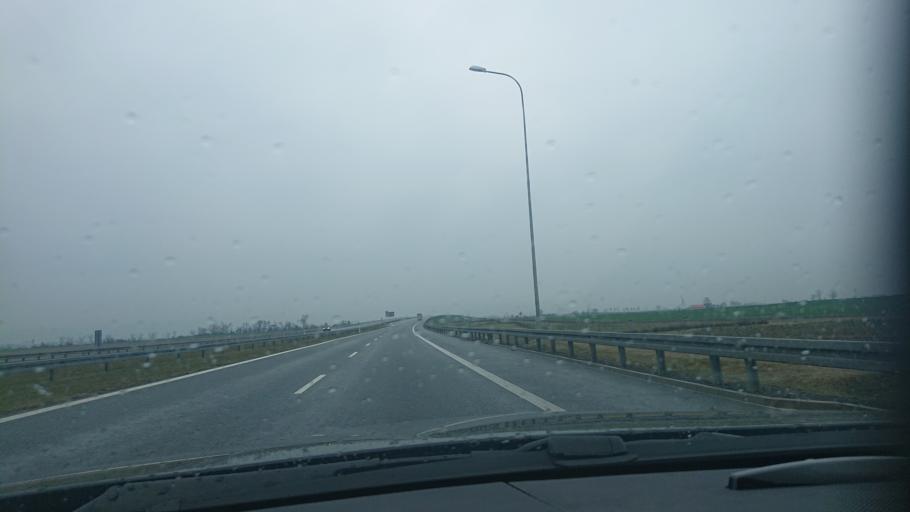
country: PL
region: Greater Poland Voivodeship
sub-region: Powiat gnieznienski
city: Gniezno
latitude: 52.5585
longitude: 17.5463
